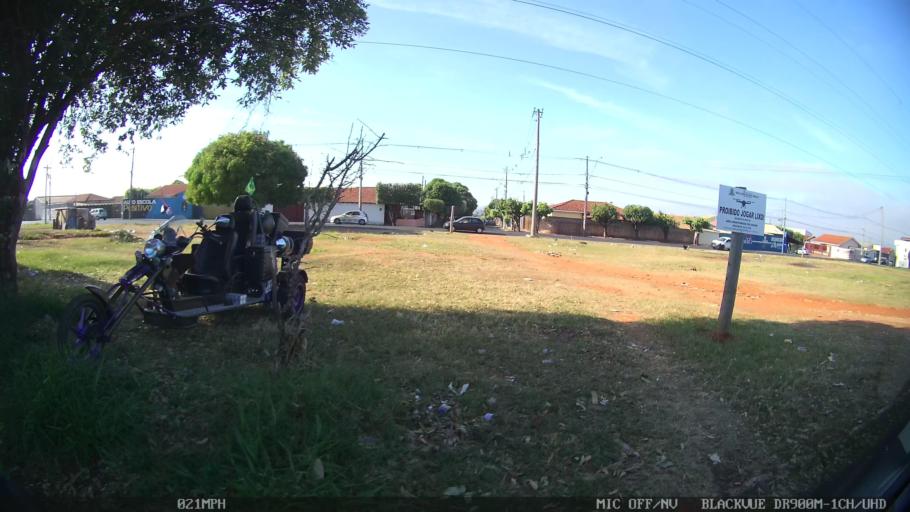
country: BR
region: Sao Paulo
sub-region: Sao Jose Do Rio Preto
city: Sao Jose do Rio Preto
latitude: -20.7818
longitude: -49.4064
